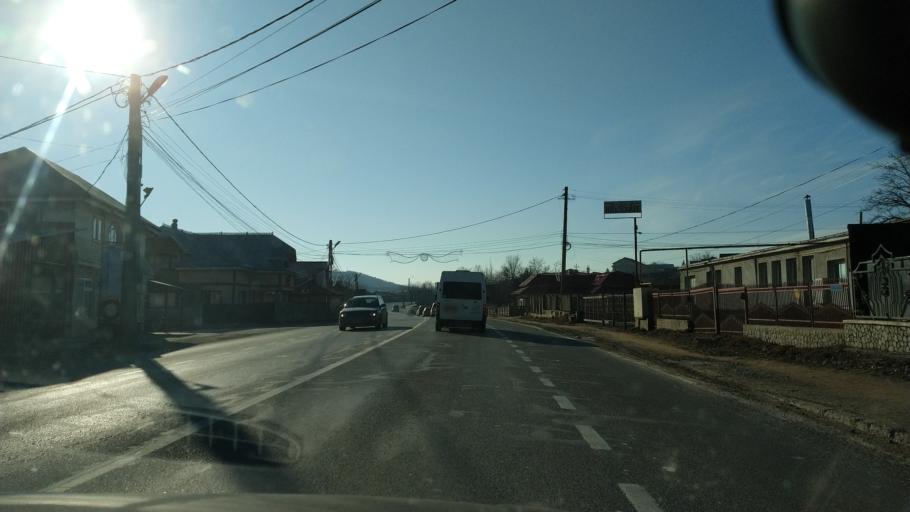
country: RO
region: Iasi
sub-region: Comuna Ion Neculce
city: Buznea
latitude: 47.2134
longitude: 27.0258
